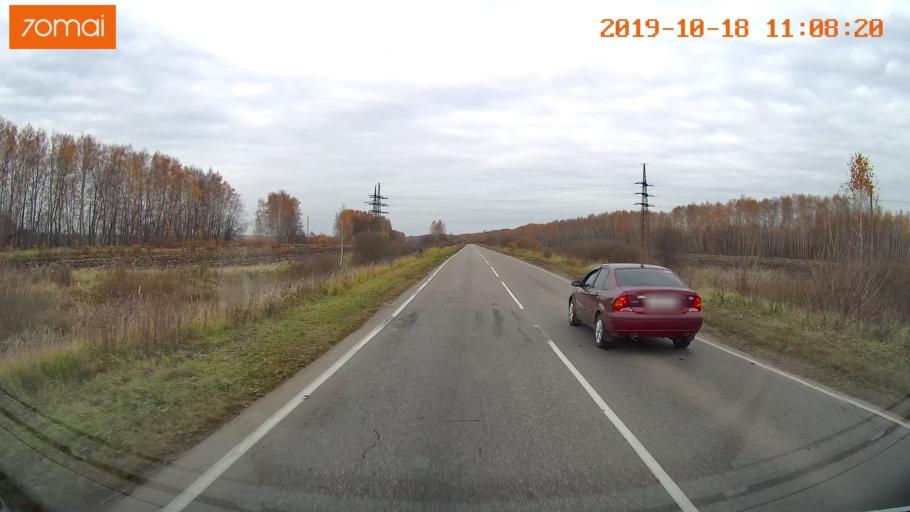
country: RU
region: Tula
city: Kimovsk
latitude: 53.9364
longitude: 38.5377
